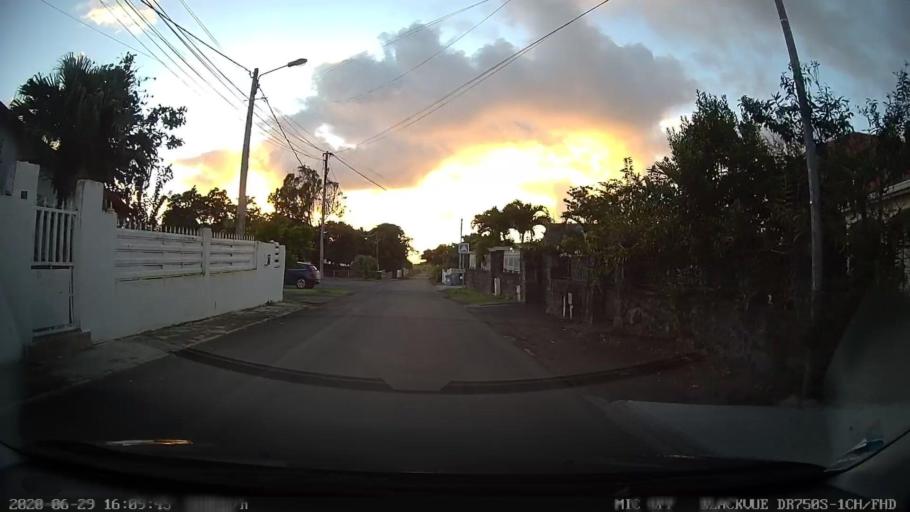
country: RE
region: Reunion
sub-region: Reunion
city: Bras-Panon
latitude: -20.9921
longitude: 55.6823
